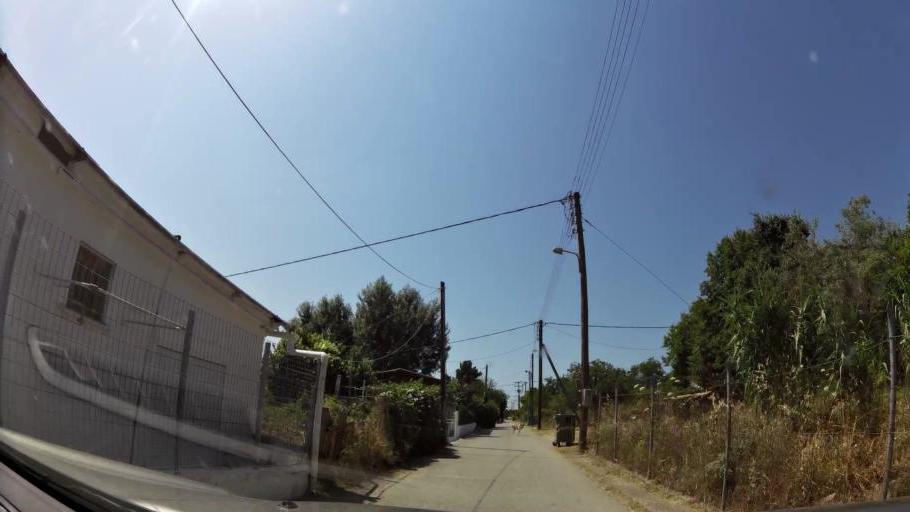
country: GR
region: Central Macedonia
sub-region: Nomos Thessalonikis
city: Neoi Epivates
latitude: 40.4966
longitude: 22.8941
